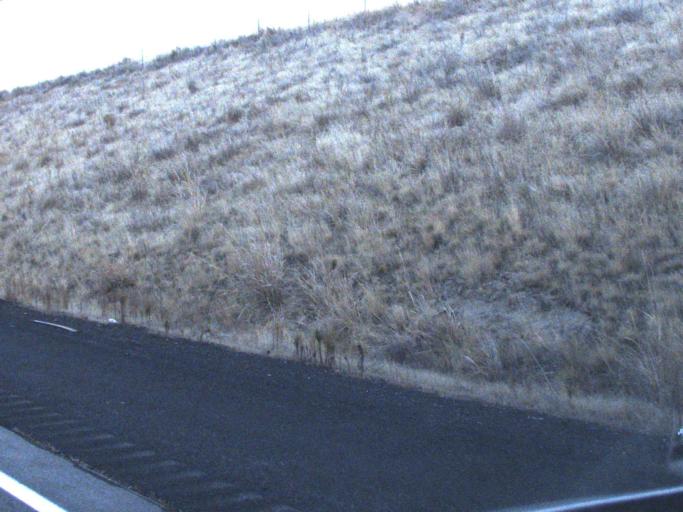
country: US
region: Washington
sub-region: Franklin County
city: Connell
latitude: 46.8835
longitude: -118.6191
